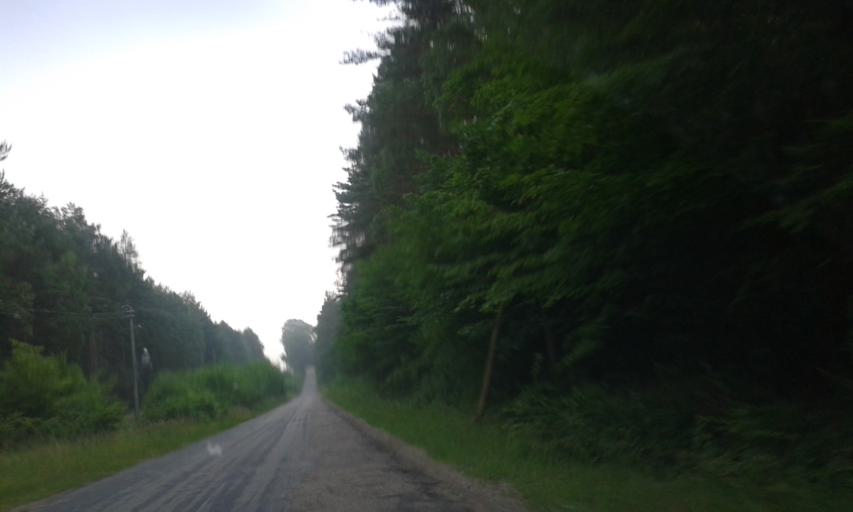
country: PL
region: Kujawsko-Pomorskie
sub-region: Powiat sepolenski
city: Sypniewo
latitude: 53.4495
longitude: 17.4026
